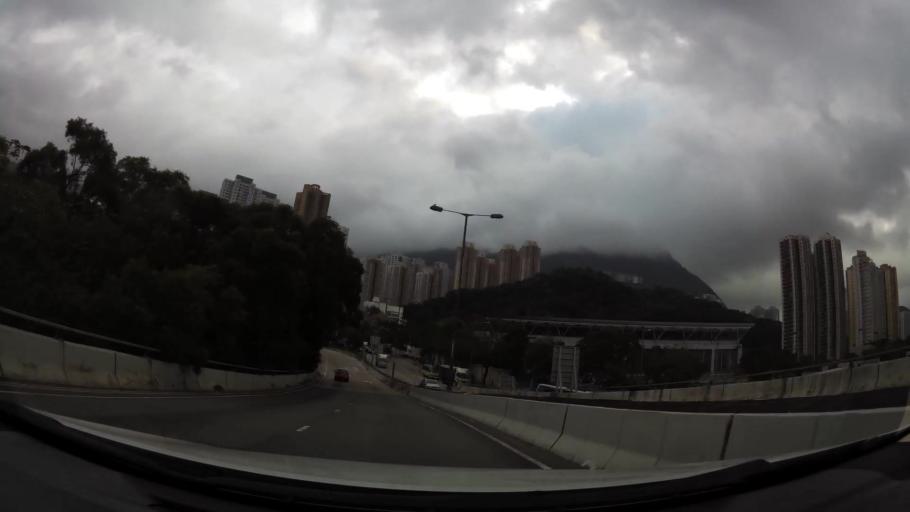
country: HK
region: Wong Tai Sin
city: Wong Tai Sin
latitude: 22.3380
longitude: 114.2053
